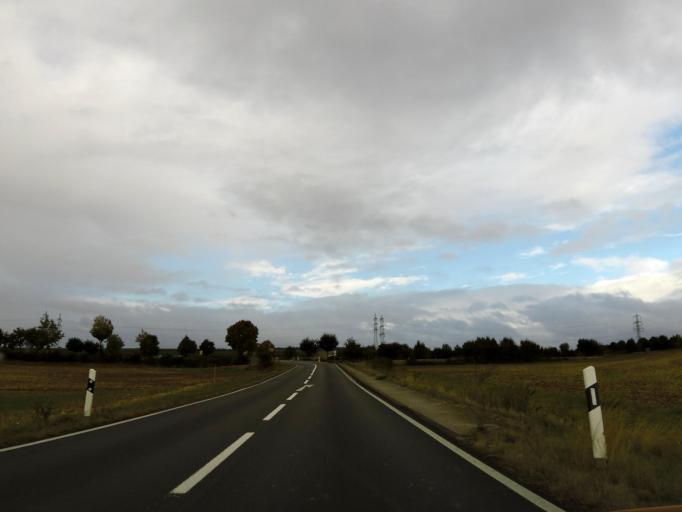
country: DE
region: Rheinland-Pfalz
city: Windesheim
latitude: 49.8837
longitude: 7.8200
